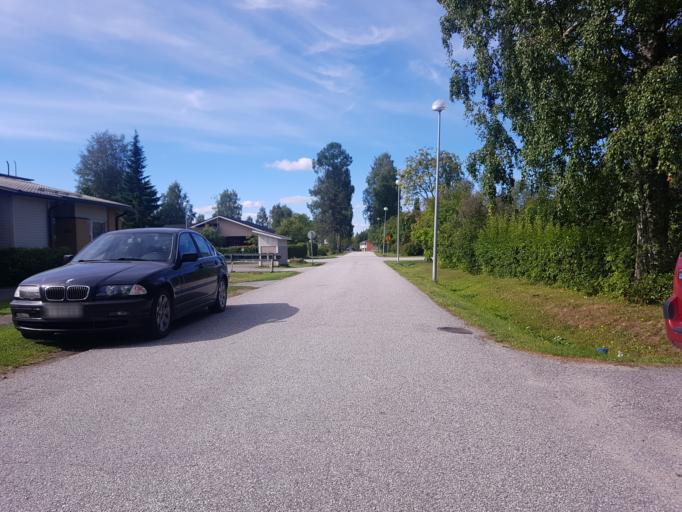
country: FI
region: Kainuu
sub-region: Kehys-Kainuu
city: Kuhmo
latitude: 64.1245
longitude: 29.5223
